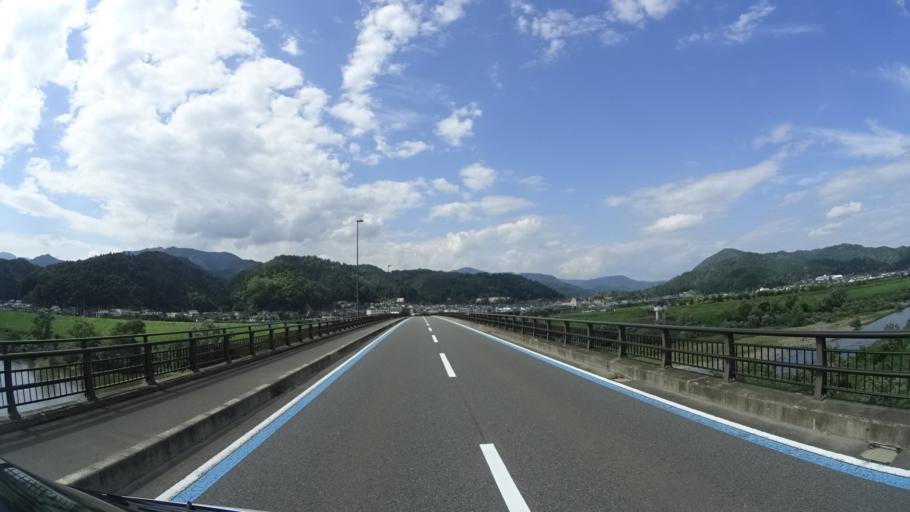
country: JP
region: Kyoto
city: Fukuchiyama
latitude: 35.3831
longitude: 135.1476
